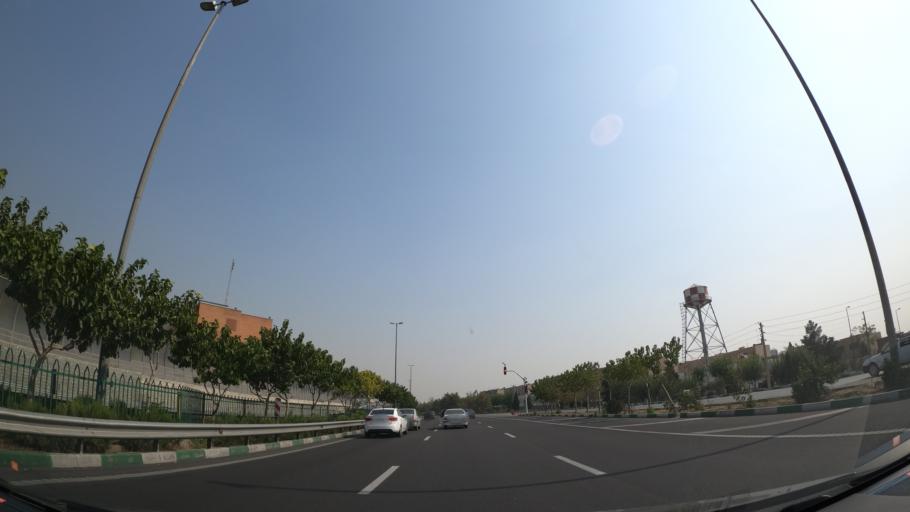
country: IR
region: Tehran
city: Shahr-e Qods
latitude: 35.7581
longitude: 51.2604
